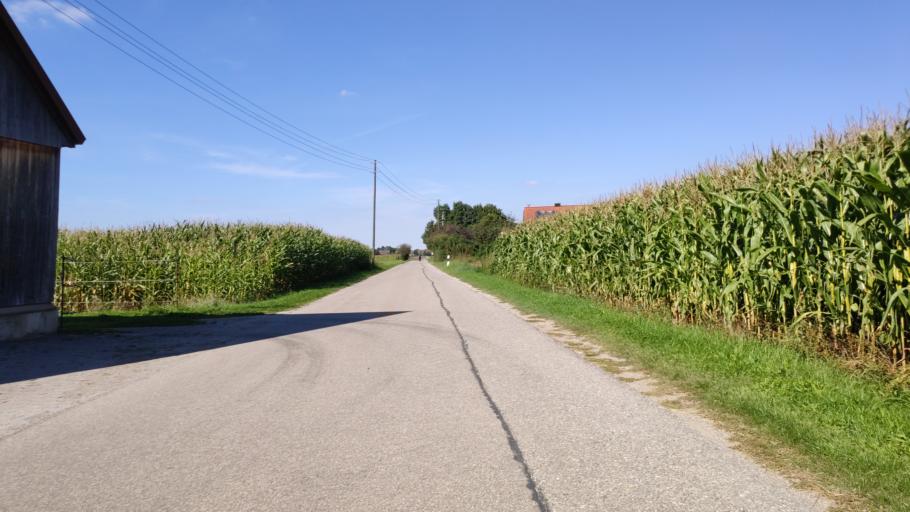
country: DE
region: Bavaria
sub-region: Swabia
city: Konigsbrunn
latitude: 48.2438
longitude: 10.9035
